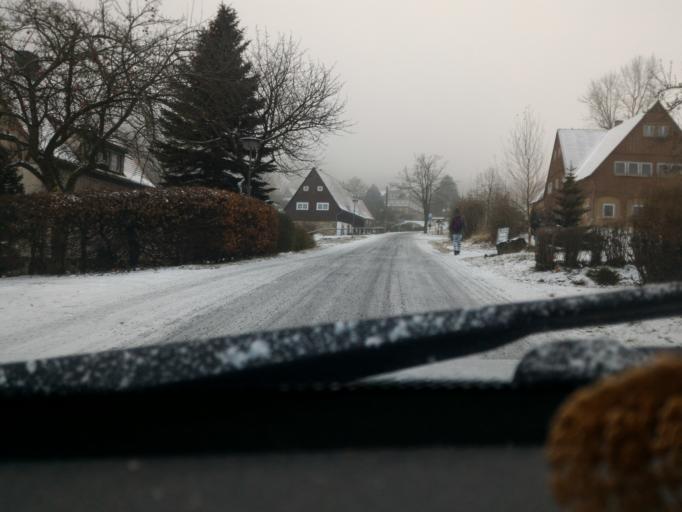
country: DE
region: Saxony
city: Grossschonau
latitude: 50.8548
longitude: 14.6543
